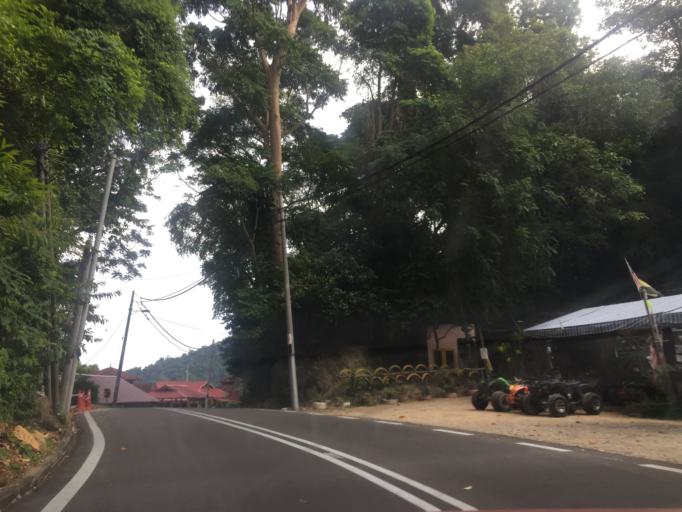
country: MY
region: Perak
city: Lumut
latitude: 4.2345
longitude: 100.5457
